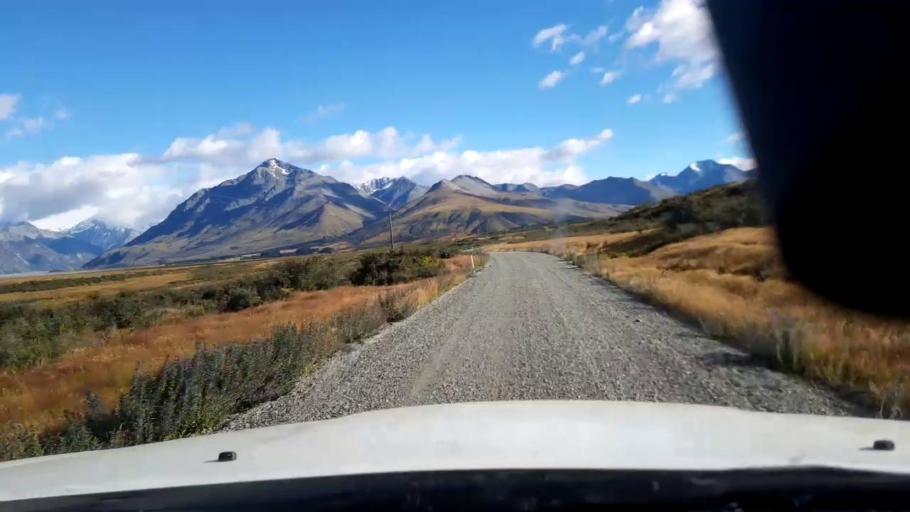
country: NZ
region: Canterbury
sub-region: Timaru District
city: Pleasant Point
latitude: -43.7470
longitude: 170.5715
